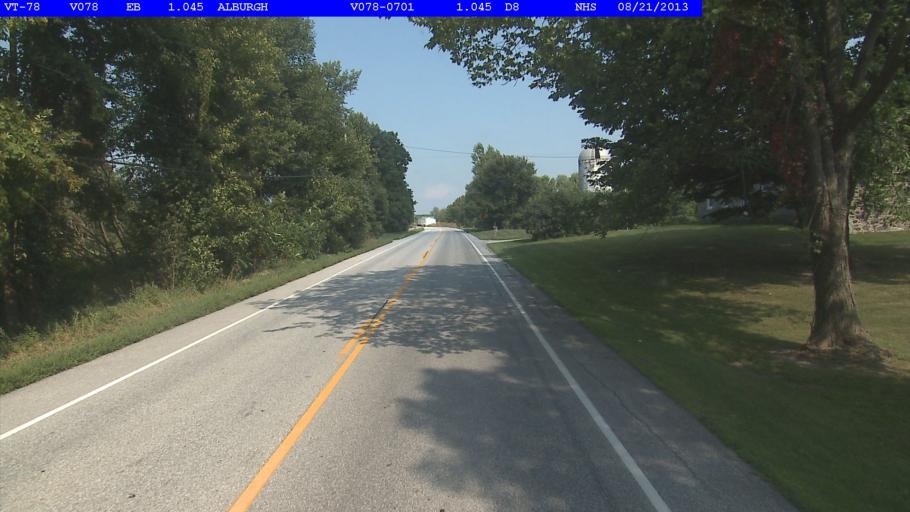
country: US
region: New York
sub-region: Clinton County
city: Rouses Point
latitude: 44.9705
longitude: -73.2626
